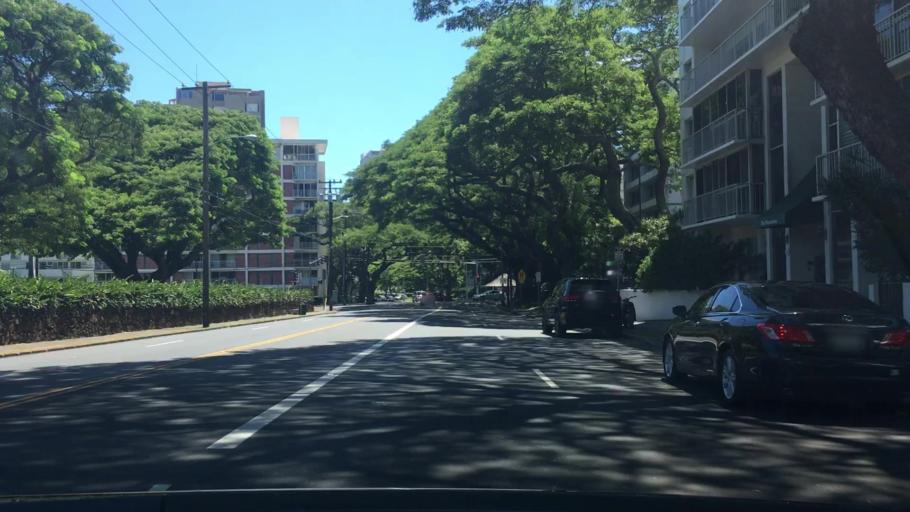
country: US
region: Hawaii
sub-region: Honolulu County
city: Honolulu
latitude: 21.3037
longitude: -157.8317
